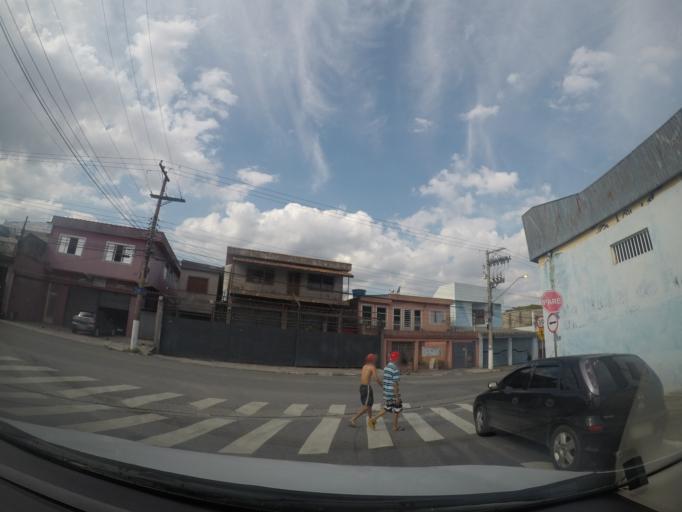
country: BR
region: Sao Paulo
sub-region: Guarulhos
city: Guarulhos
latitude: -23.4531
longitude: -46.5068
